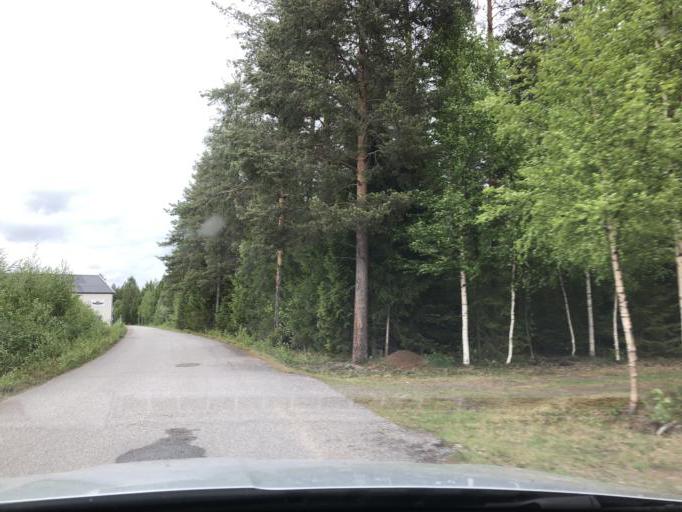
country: SE
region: Norrbotten
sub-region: Pitea Kommun
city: Roknas
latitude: 65.3904
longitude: 21.2697
